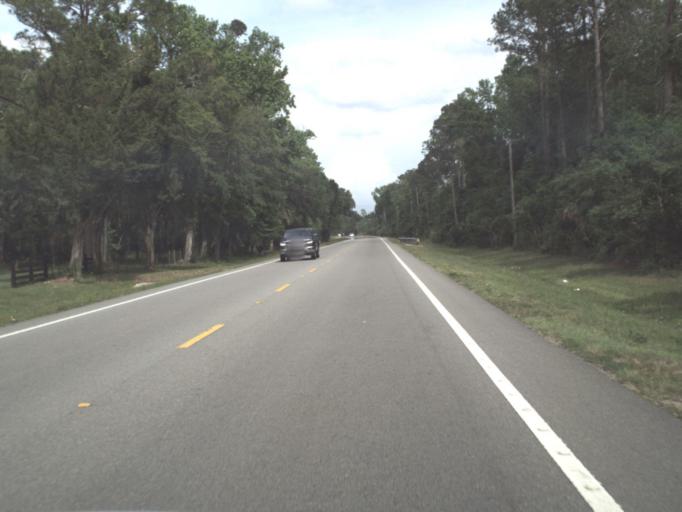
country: US
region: Florida
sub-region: Flagler County
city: Bunnell
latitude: 29.4671
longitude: -81.2932
